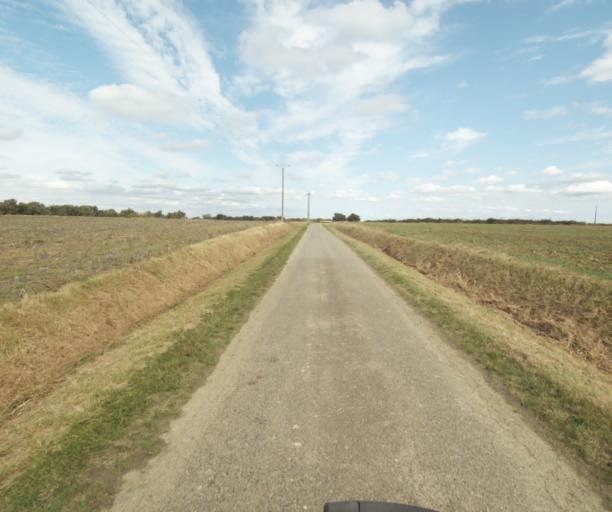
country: FR
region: Midi-Pyrenees
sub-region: Departement du Tarn-et-Garonne
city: Finhan
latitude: 43.8793
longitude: 1.1774
